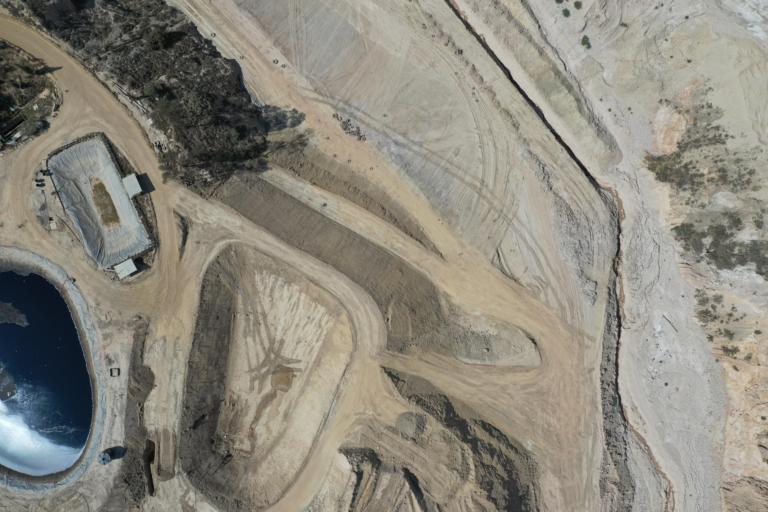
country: BO
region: La Paz
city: La Paz
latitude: -16.5613
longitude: -68.1279
